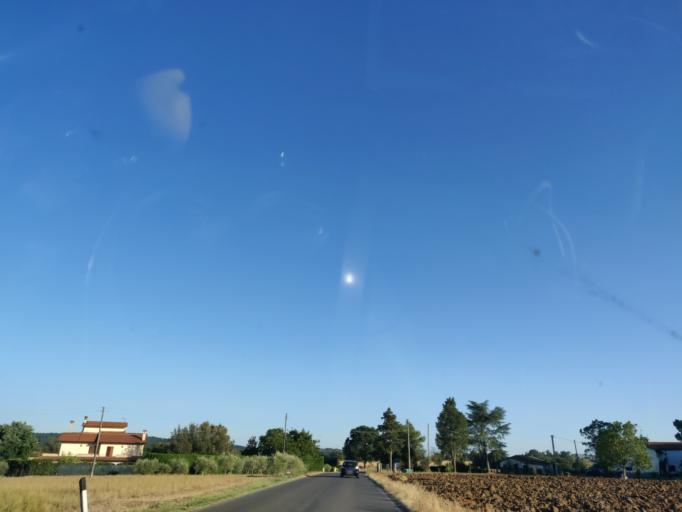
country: IT
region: Latium
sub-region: Provincia di Viterbo
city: Acquapendente
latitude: 42.7200
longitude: 11.8752
